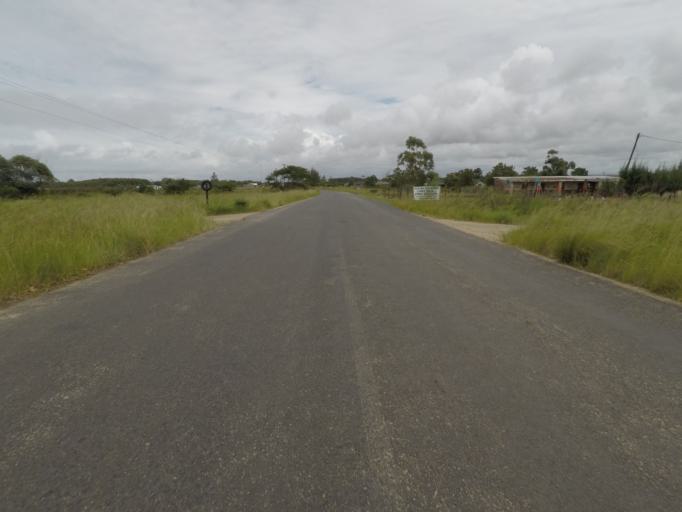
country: ZA
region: KwaZulu-Natal
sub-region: uThungulu District Municipality
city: eSikhawini
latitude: -28.9100
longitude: 31.8712
